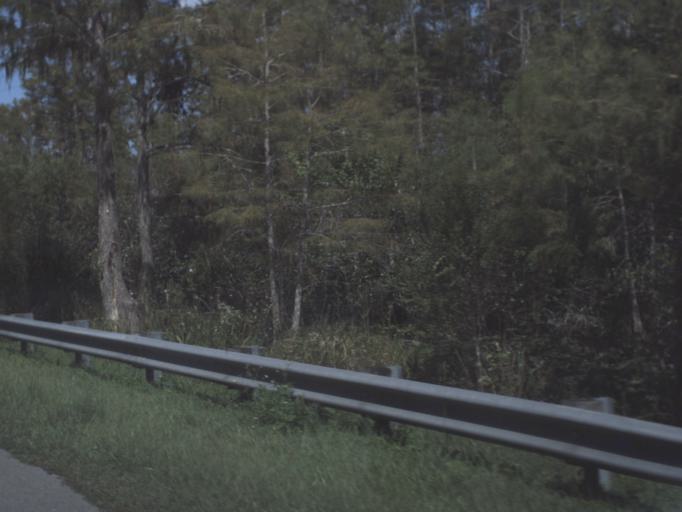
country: US
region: Florida
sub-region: Miami-Dade County
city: Kendall West
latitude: 25.8156
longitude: -80.8850
